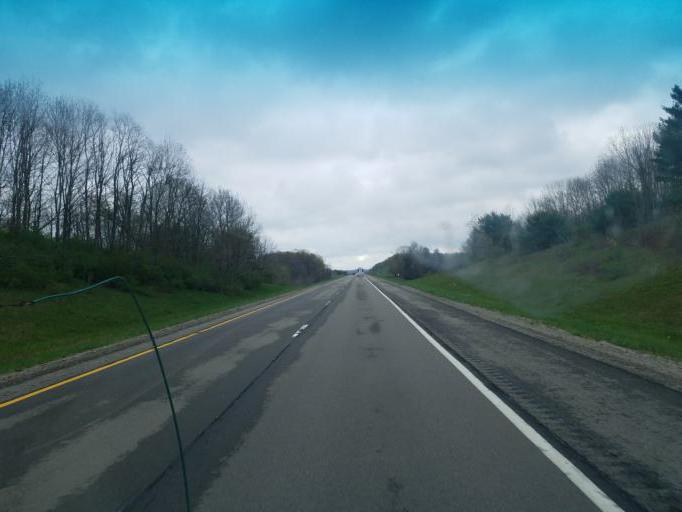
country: US
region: New York
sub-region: Chautauqua County
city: Clymer
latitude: 42.1468
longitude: -79.6379
